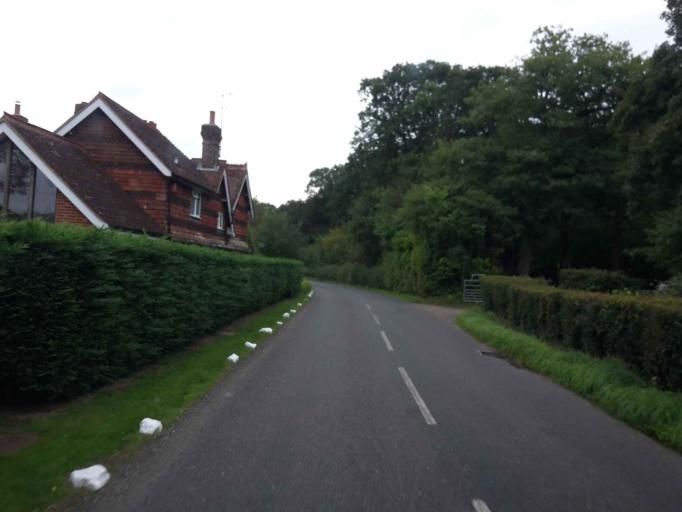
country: GB
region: England
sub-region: West Sussex
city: Rudgwick
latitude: 51.0629
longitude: -0.4454
